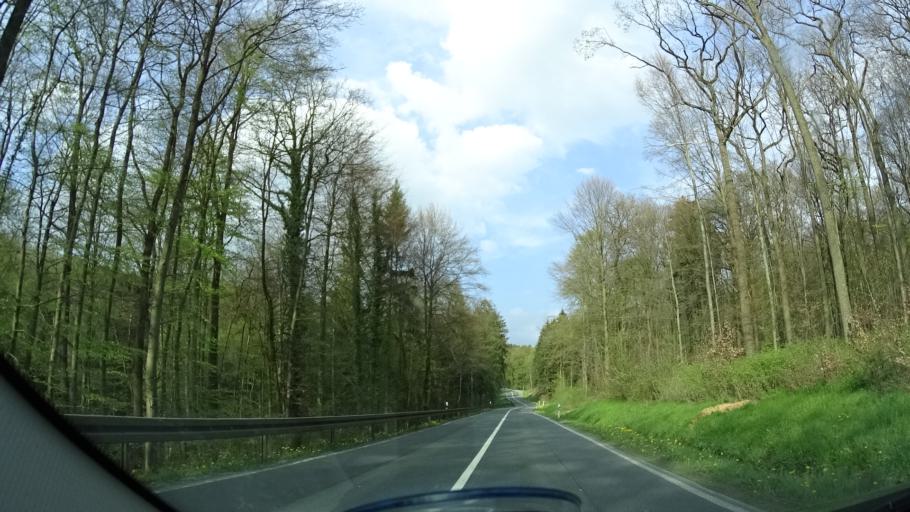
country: DE
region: North Rhine-Westphalia
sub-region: Regierungsbezirk Arnsberg
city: Ruthen
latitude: 51.4703
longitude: 8.3954
